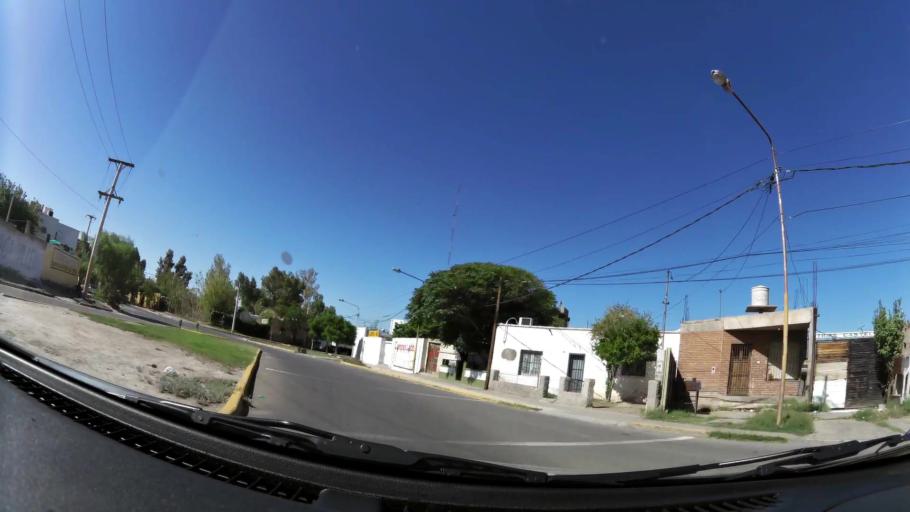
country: AR
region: San Juan
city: San Juan
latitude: -31.5443
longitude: -68.5383
